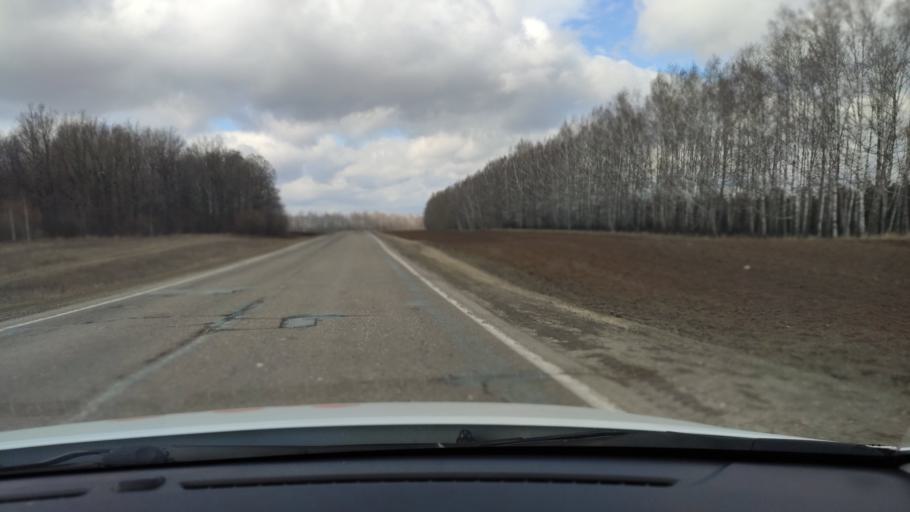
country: RU
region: Tatarstan
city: Vysokaya Gora
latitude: 56.0914
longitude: 49.1806
